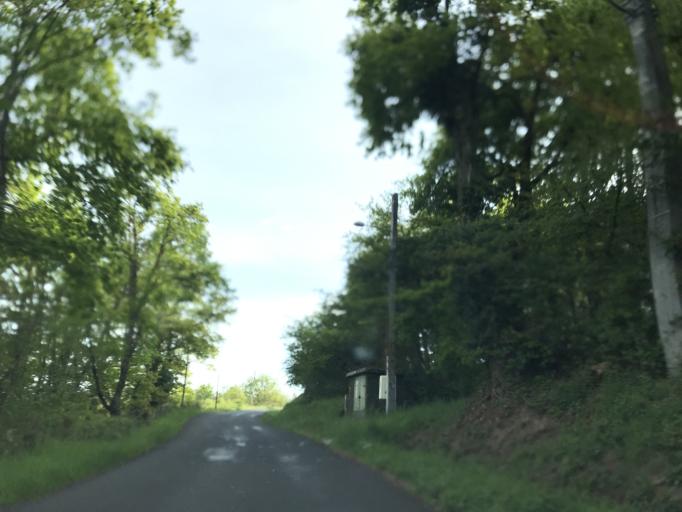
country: FR
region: Auvergne
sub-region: Departement du Puy-de-Dome
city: Courpiere
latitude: 45.7502
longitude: 3.5244
